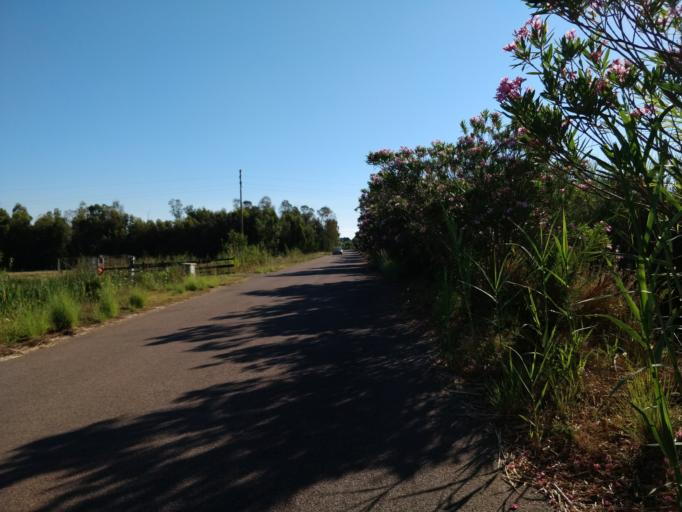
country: IT
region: Sardinia
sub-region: Provincia di Ogliastra
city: Girasole
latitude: 39.9563
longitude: 9.6745
